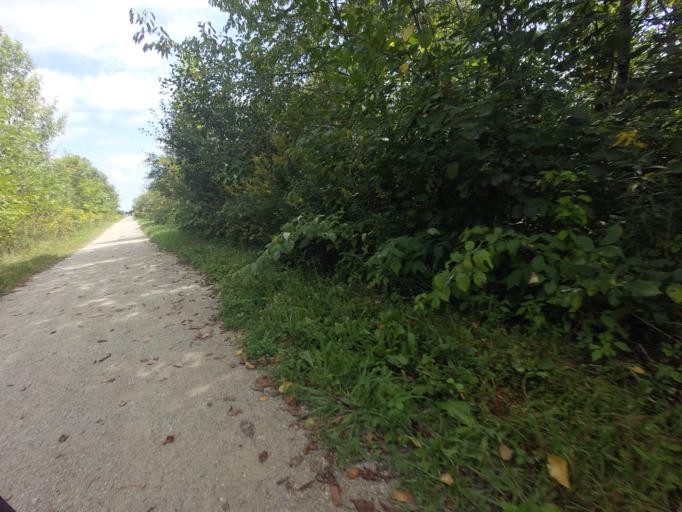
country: CA
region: Ontario
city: North Perth
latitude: 43.5759
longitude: -80.8137
